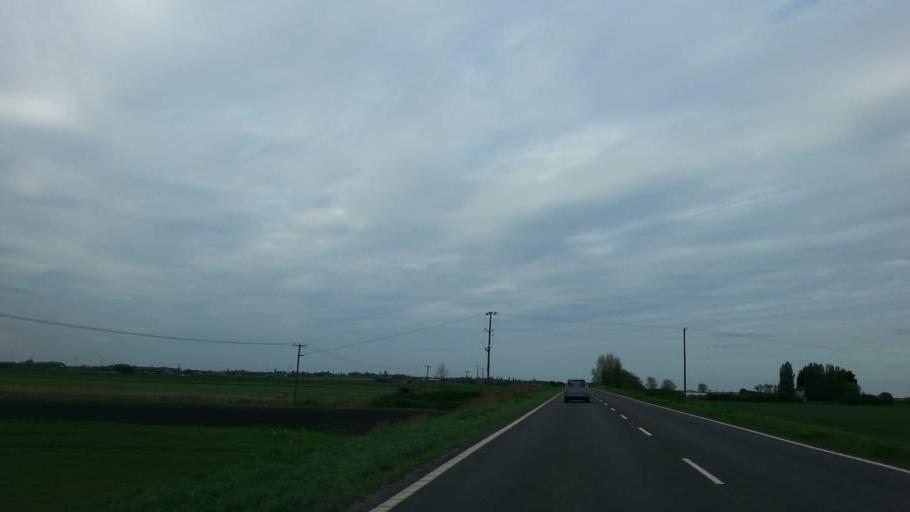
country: GB
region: England
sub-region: Cambridgeshire
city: Chatteris
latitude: 52.4704
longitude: 0.0480
